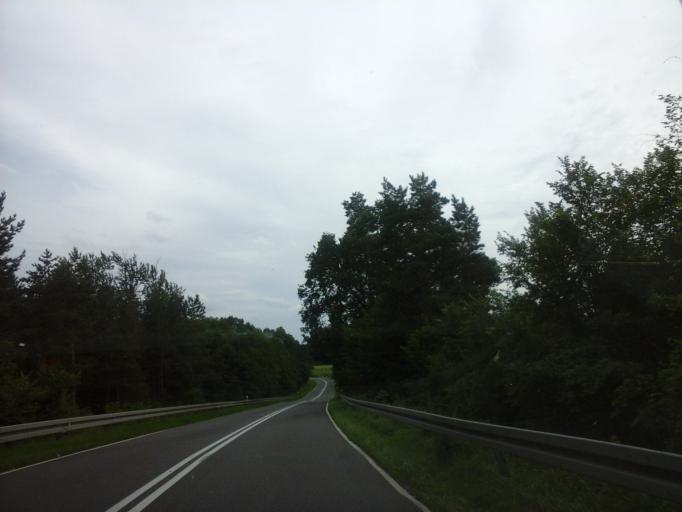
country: PL
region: West Pomeranian Voivodeship
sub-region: Powiat stargardzki
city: Suchan
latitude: 53.2582
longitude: 15.3330
